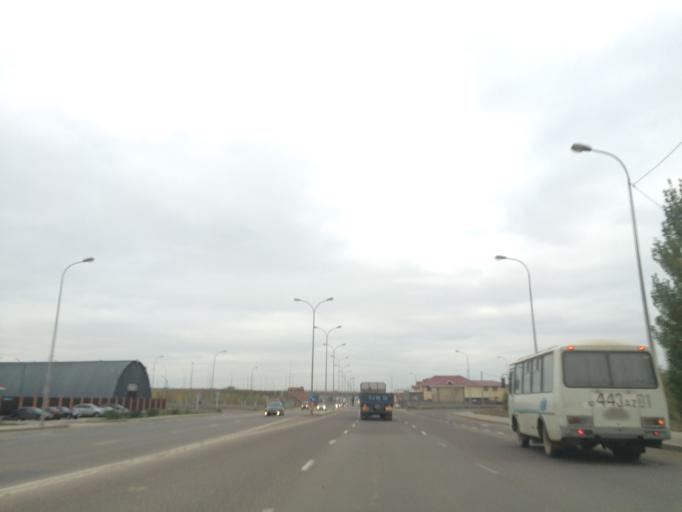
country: KZ
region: Astana Qalasy
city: Astana
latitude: 51.1718
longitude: 71.4882
